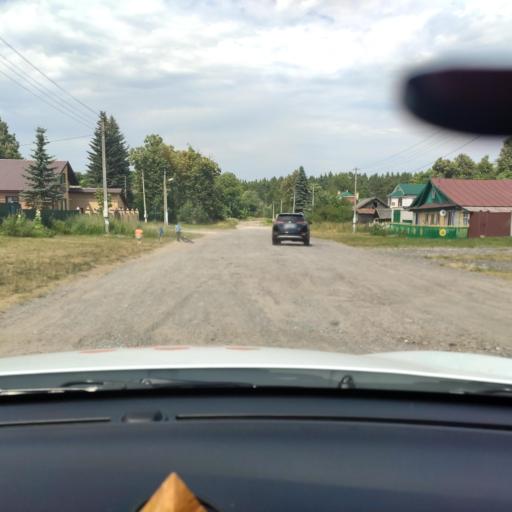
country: RU
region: Tatarstan
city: Osinovo
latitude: 55.9083
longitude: 48.9622
